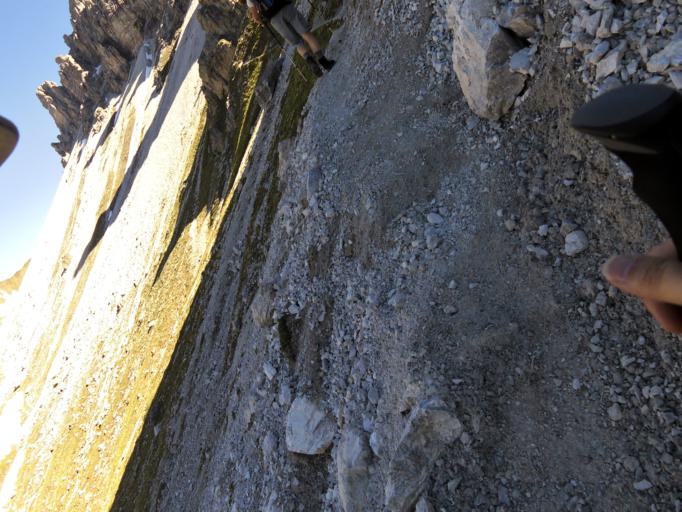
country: AT
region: Tyrol
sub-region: Politischer Bezirk Innsbruck Land
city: Neustift im Stubaital
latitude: 47.1386
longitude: 11.2748
